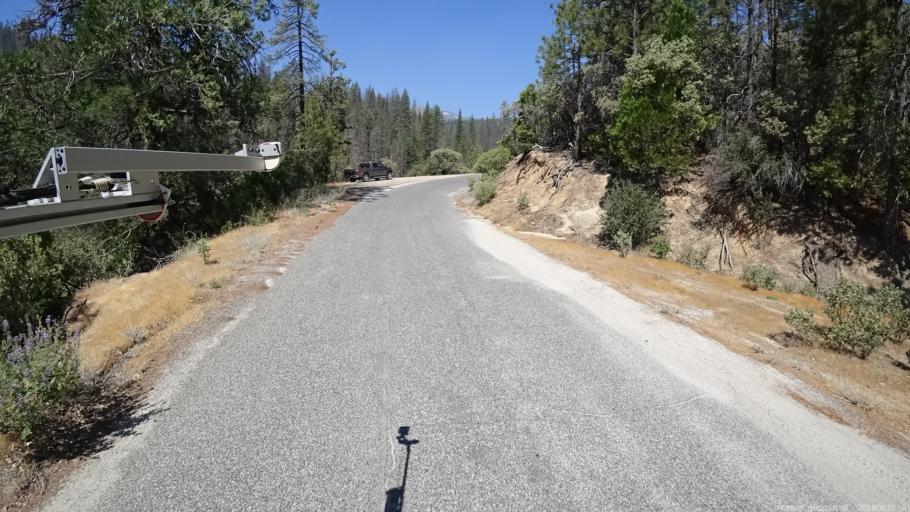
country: US
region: California
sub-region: Madera County
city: Oakhurst
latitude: 37.3608
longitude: -119.3507
